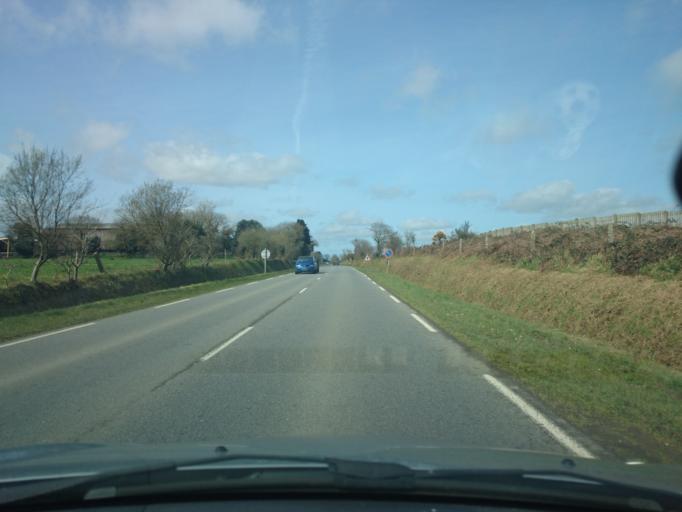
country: FR
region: Brittany
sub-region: Departement du Finistere
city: Gouesnou
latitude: 48.4413
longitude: -4.4425
